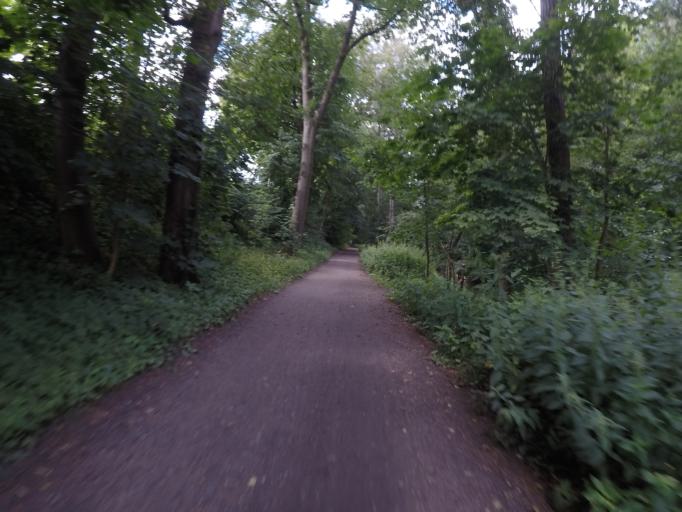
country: DE
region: Hamburg
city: Stellingen
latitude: 53.6068
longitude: 9.9363
